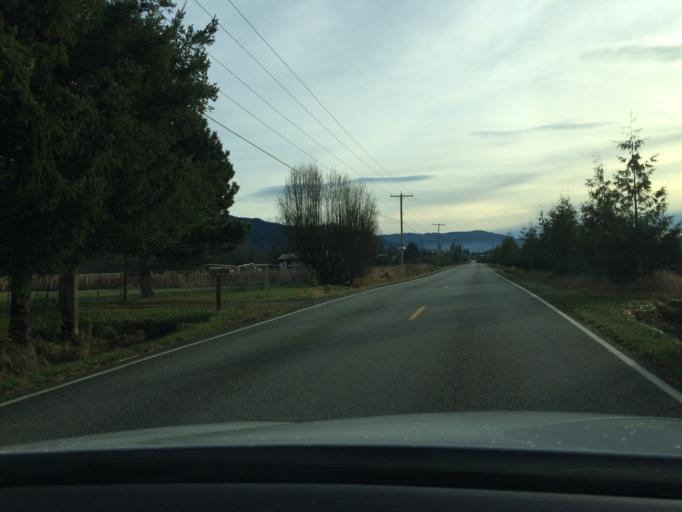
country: US
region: Washington
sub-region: Whatcom County
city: Nooksack
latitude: 48.9308
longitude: -122.2877
